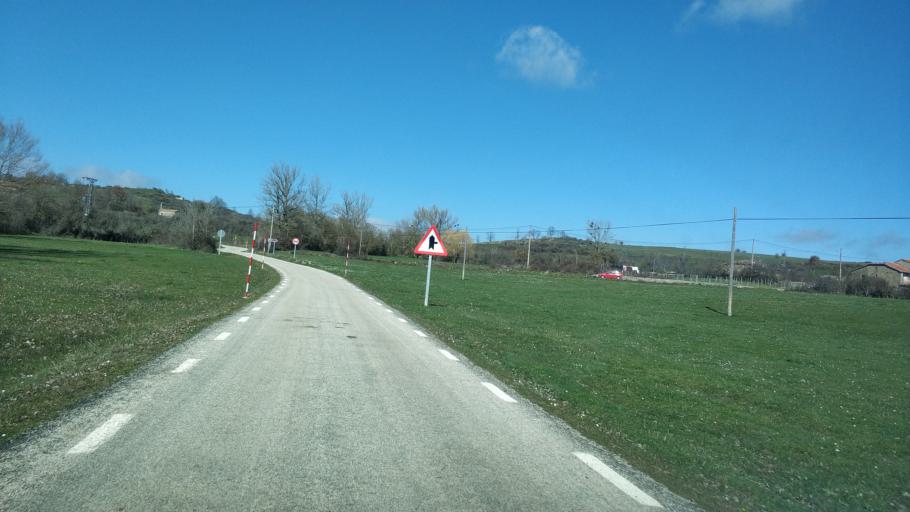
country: ES
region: Cantabria
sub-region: Provincia de Cantabria
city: Mataporquera
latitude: 42.8740
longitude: -4.0876
